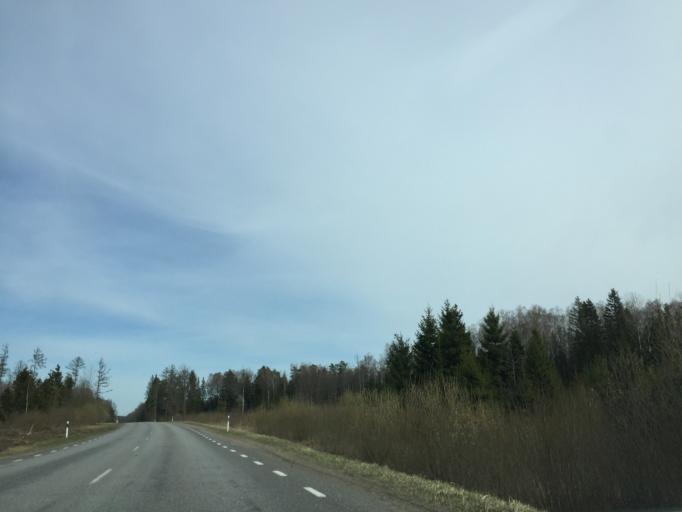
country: EE
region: Vorumaa
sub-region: Antsla vald
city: Vana-Antsla
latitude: 57.9355
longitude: 26.3588
